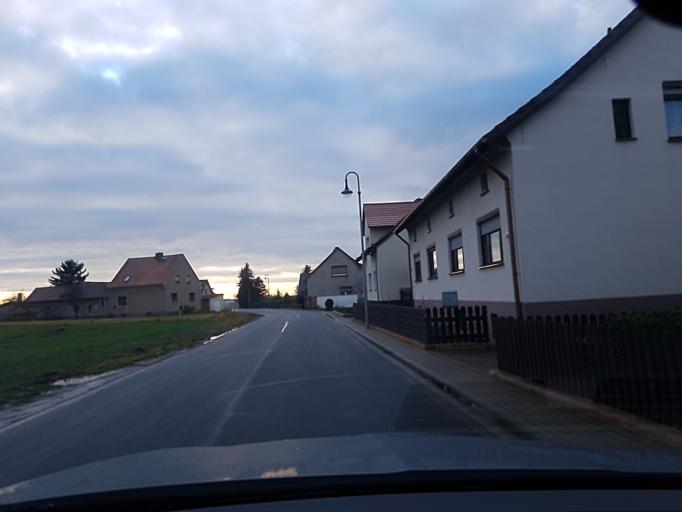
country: DE
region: Brandenburg
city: Schilda
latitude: 51.5865
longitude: 13.3836
